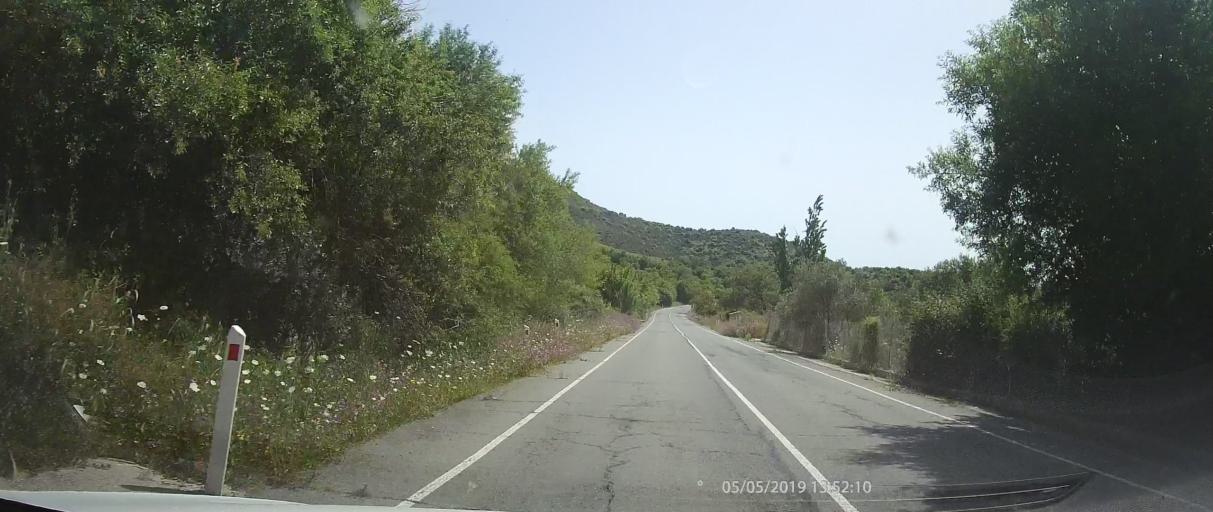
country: CY
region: Limassol
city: Pachna
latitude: 34.8318
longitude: 32.7355
